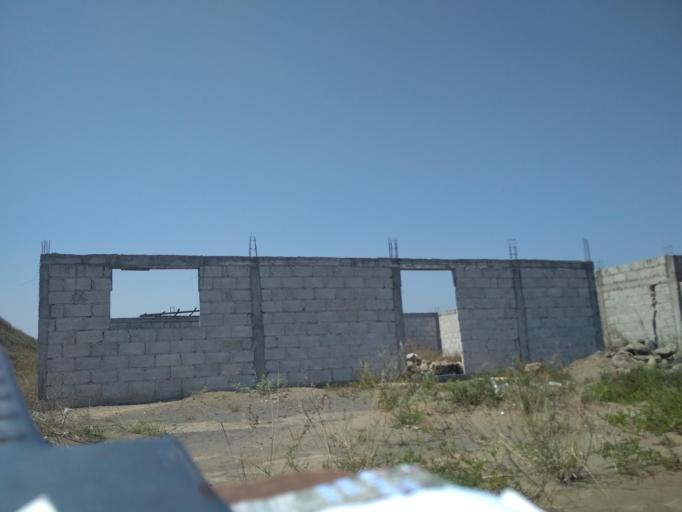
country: MX
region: Veracruz
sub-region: Veracruz
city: Lomas de Rio Medio Cuatro
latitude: 19.1901
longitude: -96.1973
